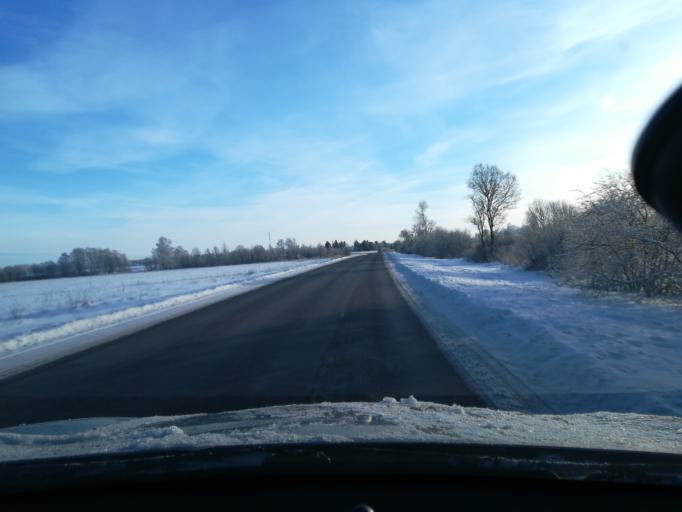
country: EE
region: Harju
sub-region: Harku vald
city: Tabasalu
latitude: 59.3727
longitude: 24.4732
